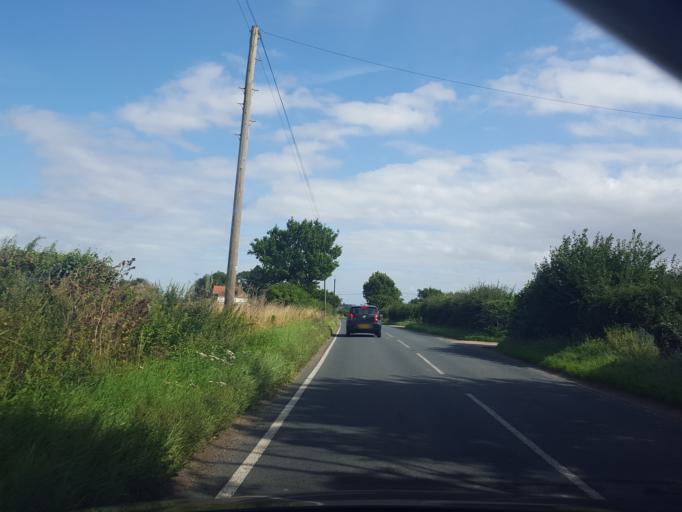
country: GB
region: England
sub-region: Suffolk
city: Shotley Gate
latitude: 51.9345
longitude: 1.2082
